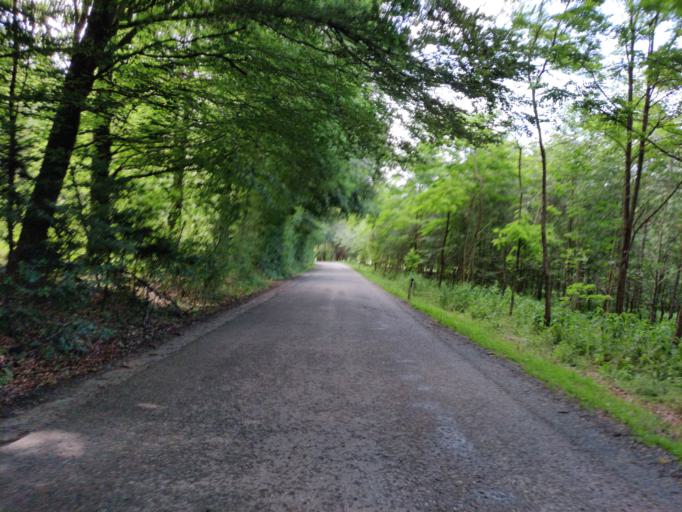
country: AT
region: Styria
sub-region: Politischer Bezirk Graz-Umgebung
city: Thal
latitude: 47.0656
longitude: 15.3407
